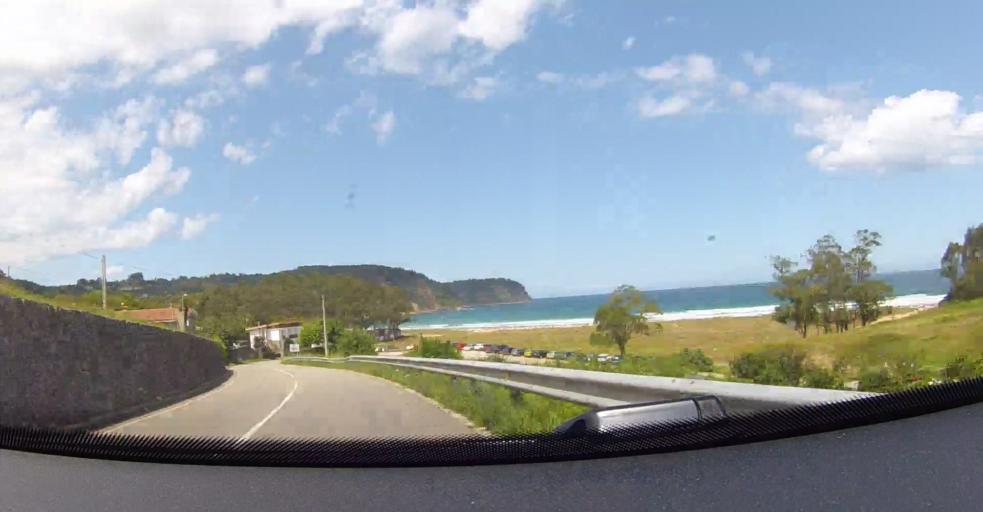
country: ES
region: Asturias
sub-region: Province of Asturias
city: Villaviciosa
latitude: 43.5312
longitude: -5.3748
